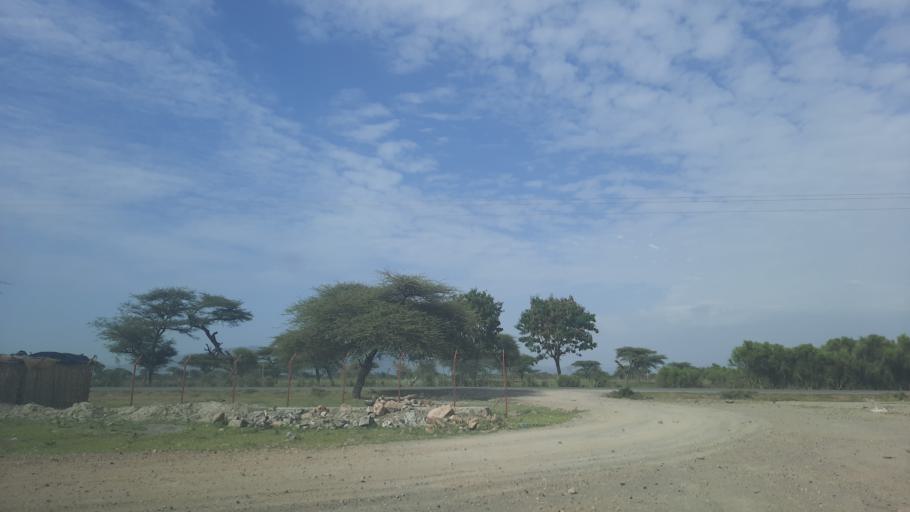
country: ET
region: Oromiya
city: Ziway
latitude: 7.6974
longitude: 38.6571
